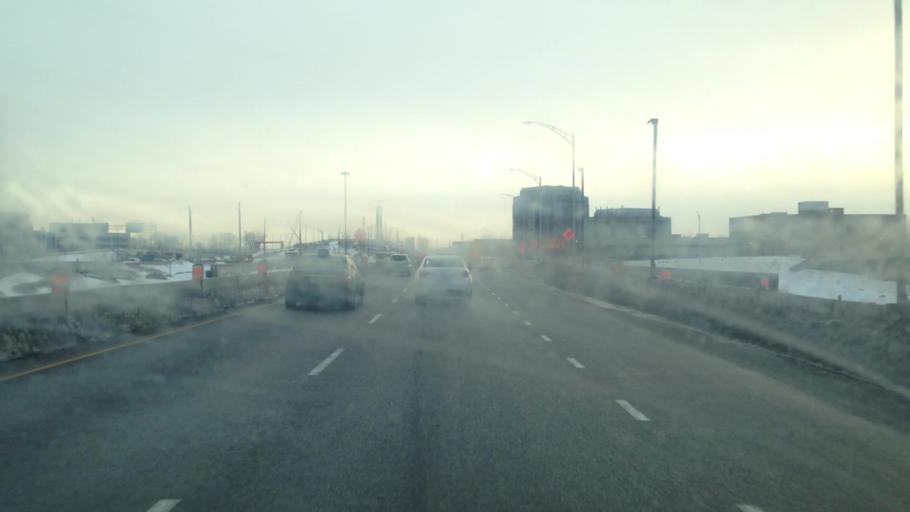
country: CA
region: Quebec
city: Westmount
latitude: 45.4705
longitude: -73.5460
